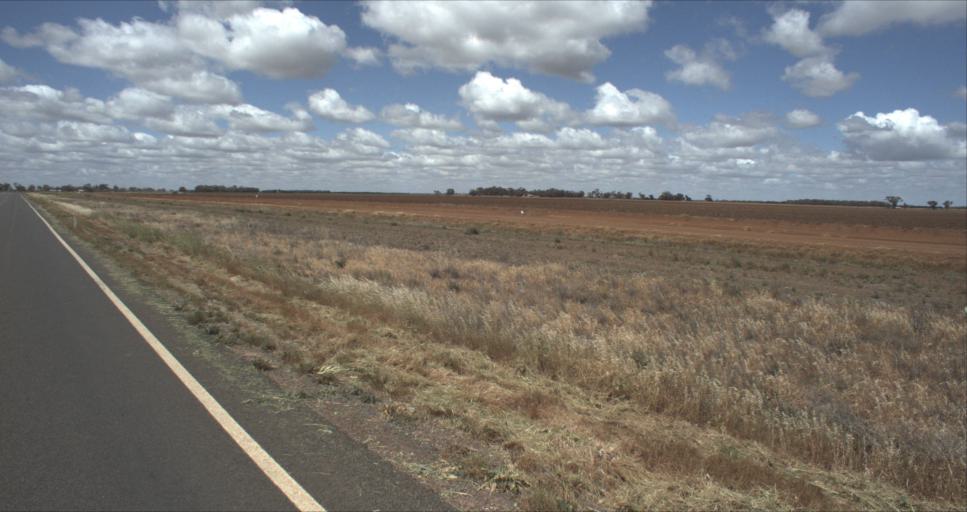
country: AU
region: New South Wales
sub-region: Murrumbidgee Shire
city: Darlington Point
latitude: -34.4719
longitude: 146.1420
